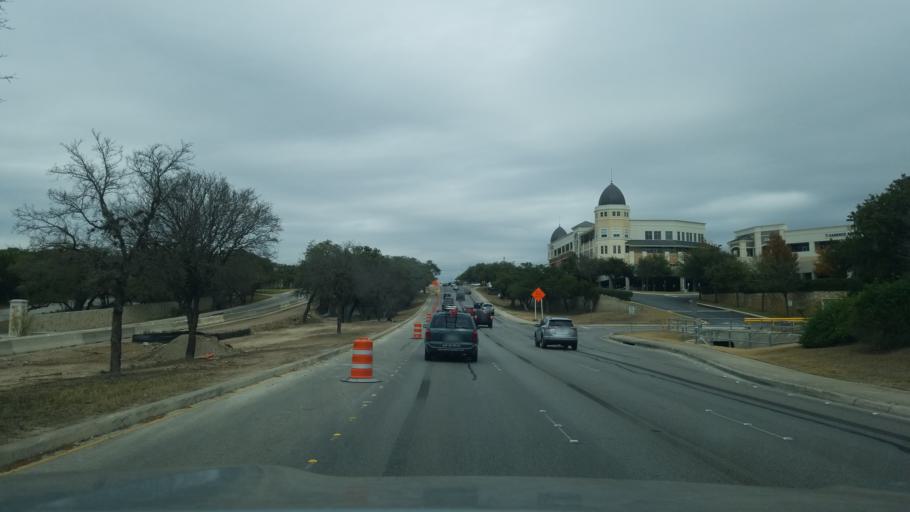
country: US
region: Texas
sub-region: Bexar County
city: Shavano Park
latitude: 29.5533
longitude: -98.5395
